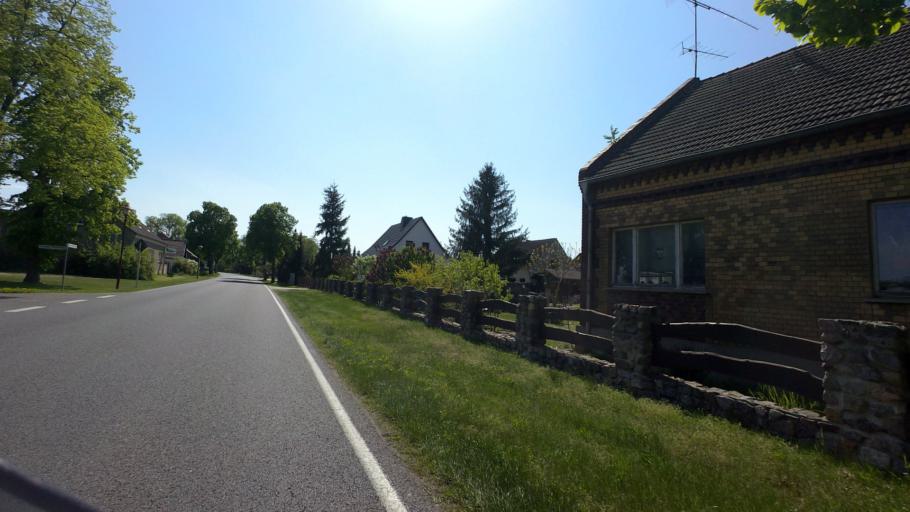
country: DE
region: Brandenburg
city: Tauche
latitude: 52.1198
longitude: 14.1921
